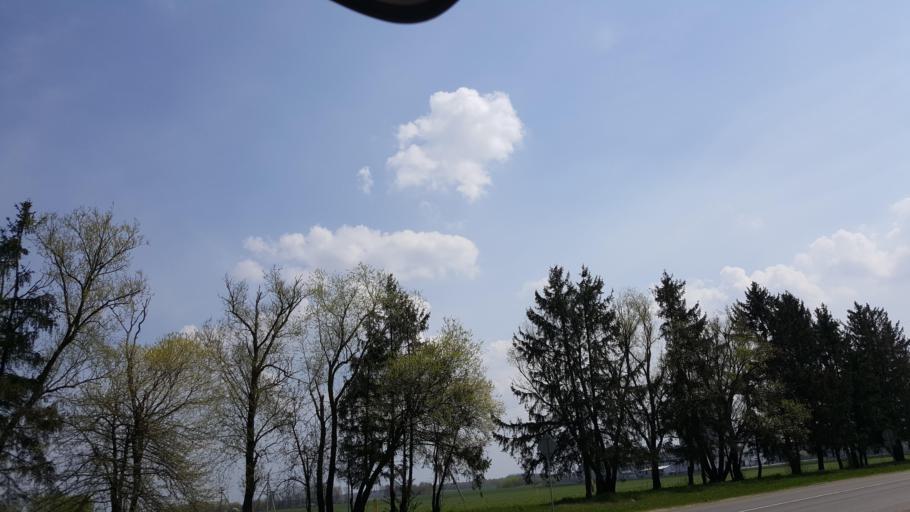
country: BY
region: Brest
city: Zhabinka
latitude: 52.2110
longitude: 24.0002
